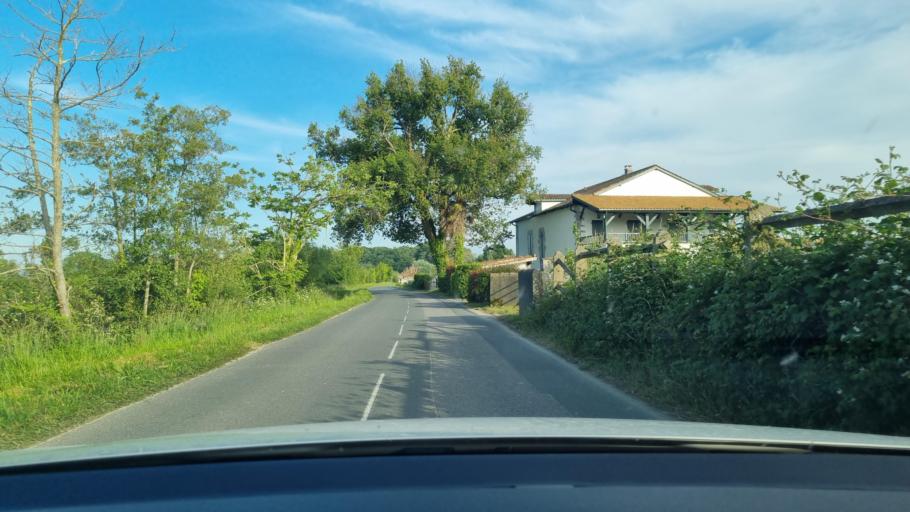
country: FR
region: Aquitaine
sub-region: Departement des Landes
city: Peyrehorade
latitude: 43.5416
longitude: -1.1644
